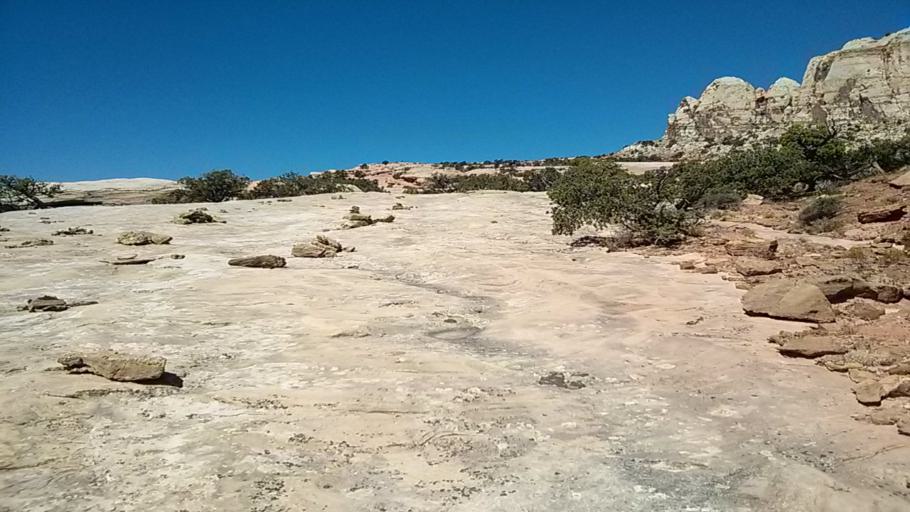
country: US
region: Utah
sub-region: Wayne County
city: Loa
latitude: 38.3046
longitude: -111.2597
